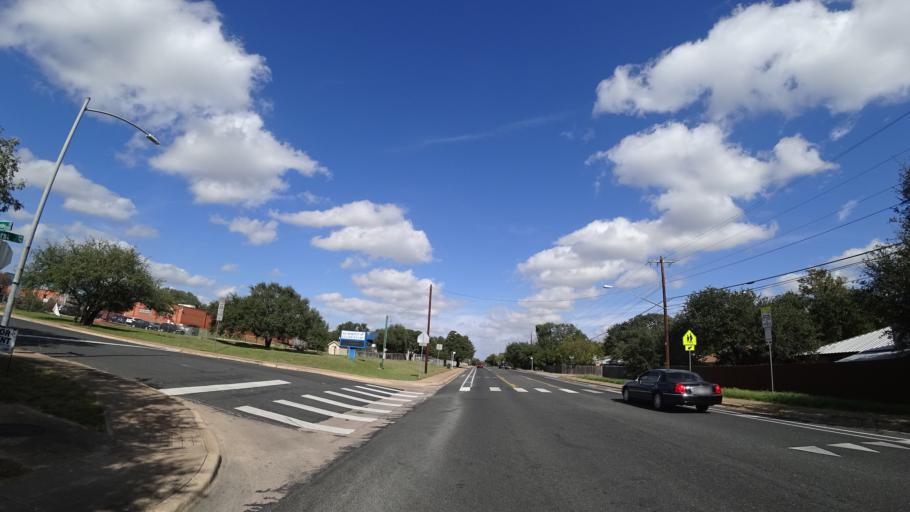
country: US
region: Texas
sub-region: Travis County
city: Wells Branch
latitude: 30.4172
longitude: -97.7184
